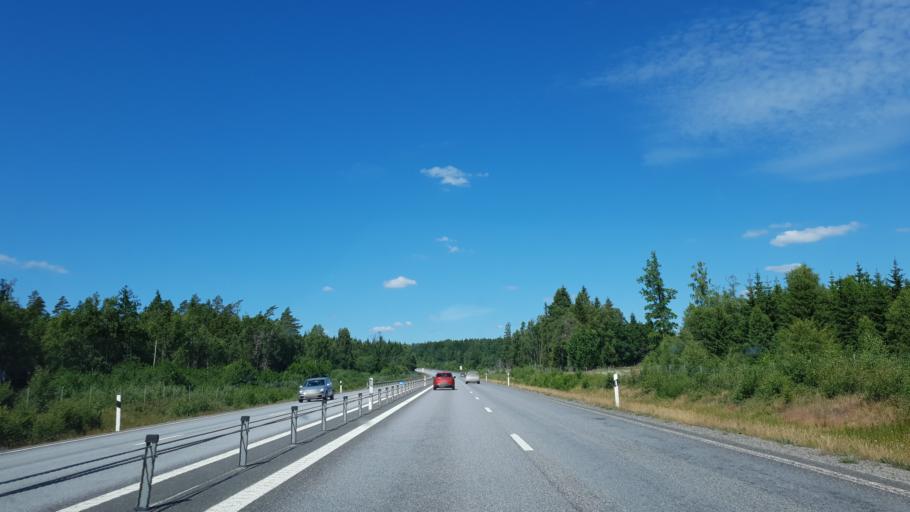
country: SE
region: Kronoberg
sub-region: Vaxjo Kommun
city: Gemla
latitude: 56.9169
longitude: 14.6183
